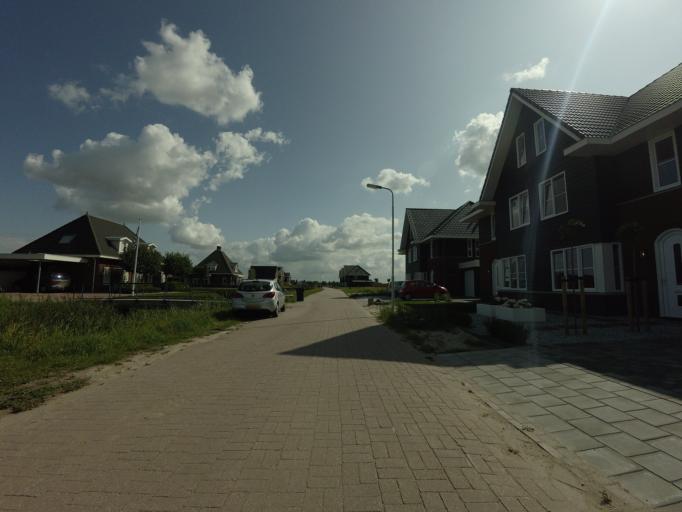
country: NL
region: Friesland
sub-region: Gemeente Het Bildt
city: Sint Annaparochie
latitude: 53.2823
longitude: 5.6576
